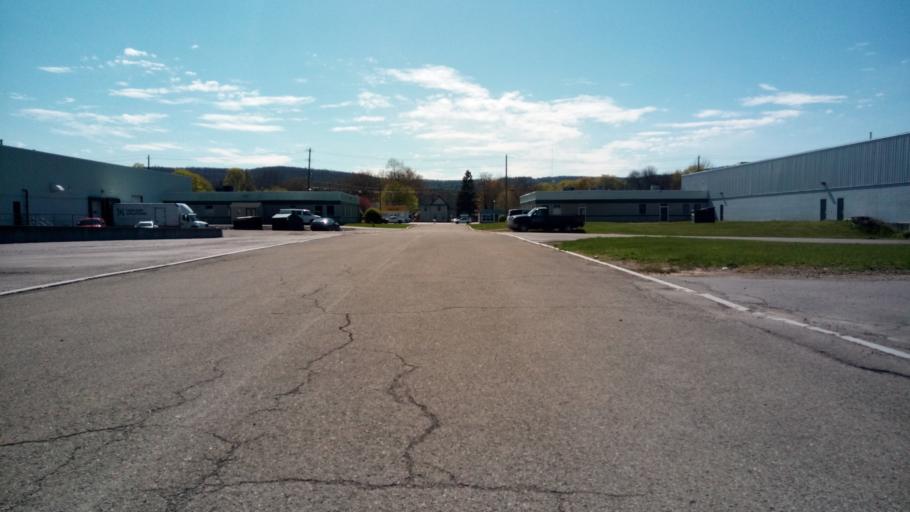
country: US
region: New York
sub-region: Chemung County
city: Elmira Heights
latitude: 42.1106
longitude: -76.8183
